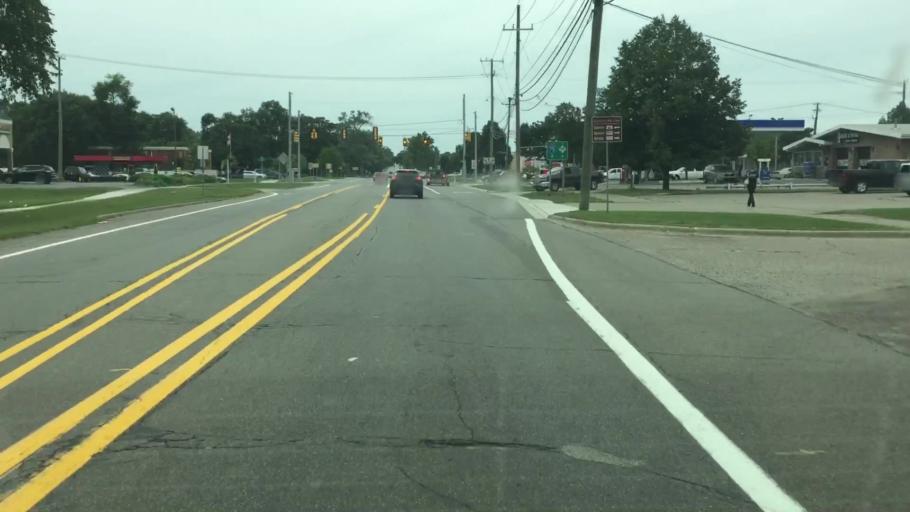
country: US
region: Michigan
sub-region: Oakland County
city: Rochester Hills
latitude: 42.6368
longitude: -83.1103
